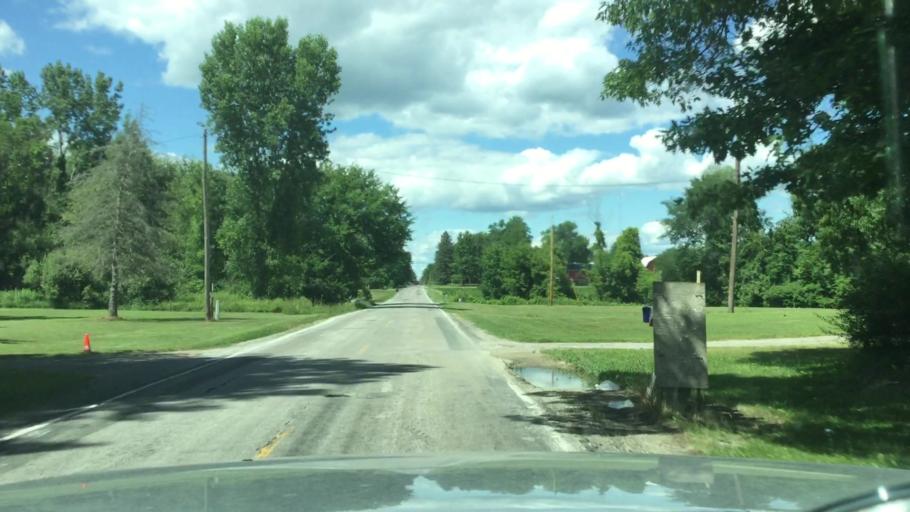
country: US
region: Michigan
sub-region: Saginaw County
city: Hemlock
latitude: 43.3708
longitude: -84.1902
